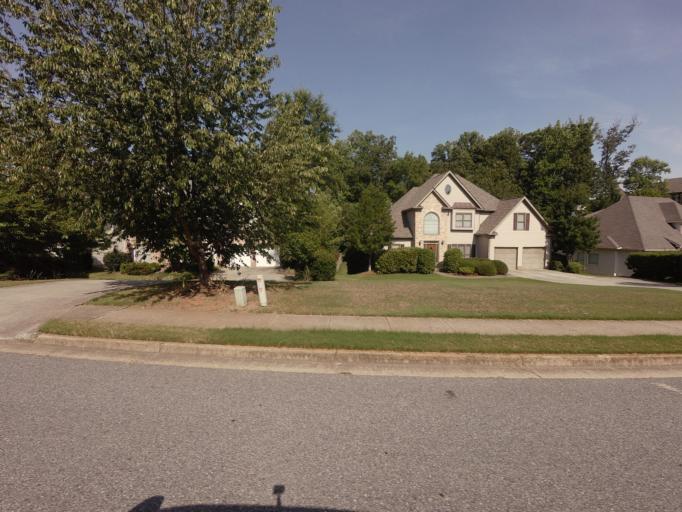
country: US
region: Georgia
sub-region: Fulton County
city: Johns Creek
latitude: 34.0830
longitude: -84.2050
